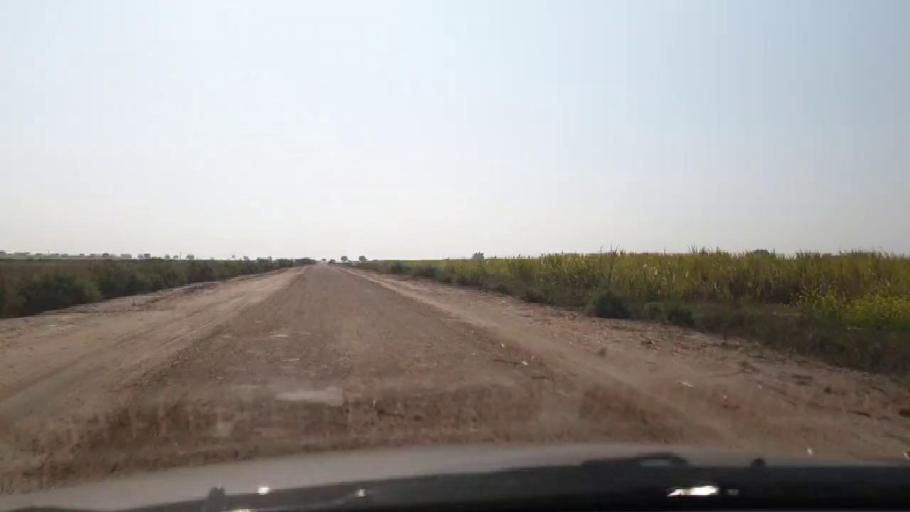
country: PK
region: Sindh
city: Jhol
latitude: 25.8668
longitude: 68.9980
